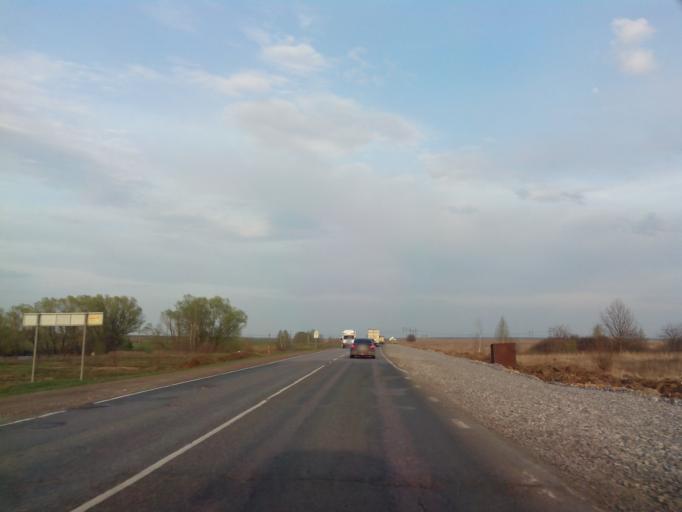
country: RU
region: Rjazan
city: Korablino
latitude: 53.7509
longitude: 39.8475
